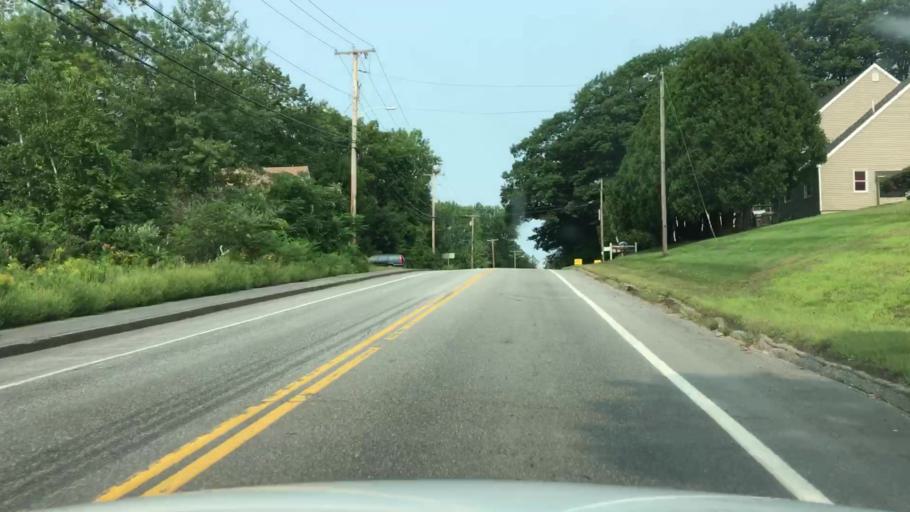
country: US
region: Maine
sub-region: Androscoggin County
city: Livermore Falls
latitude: 44.4635
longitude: -70.1800
